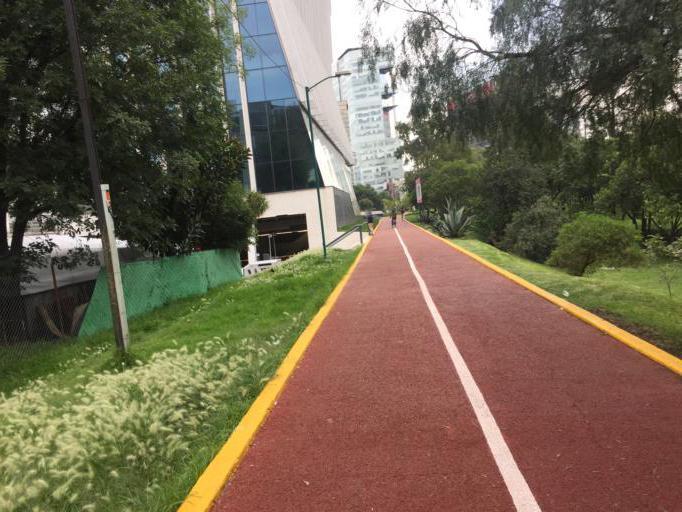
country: MX
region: Mexico City
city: Polanco
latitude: 19.4243
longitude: -99.2028
